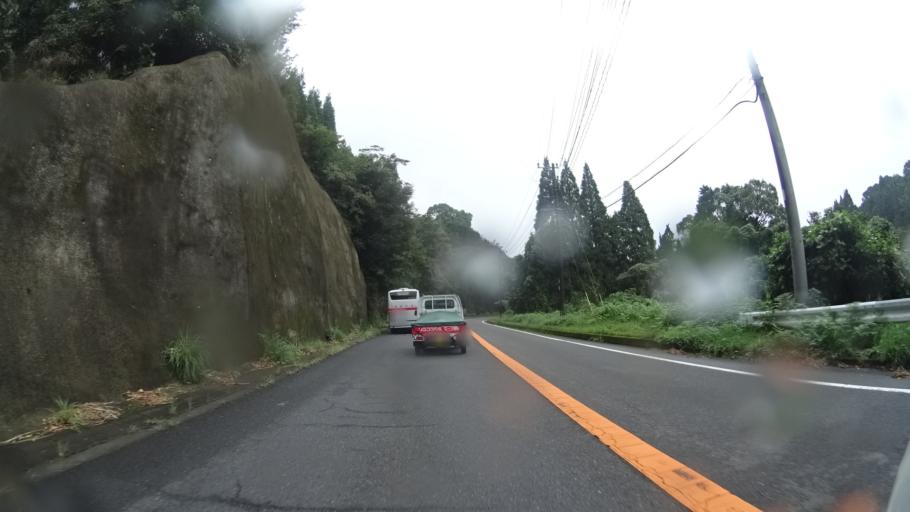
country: JP
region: Kagoshima
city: Kajiki
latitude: 31.7747
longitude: 130.6691
